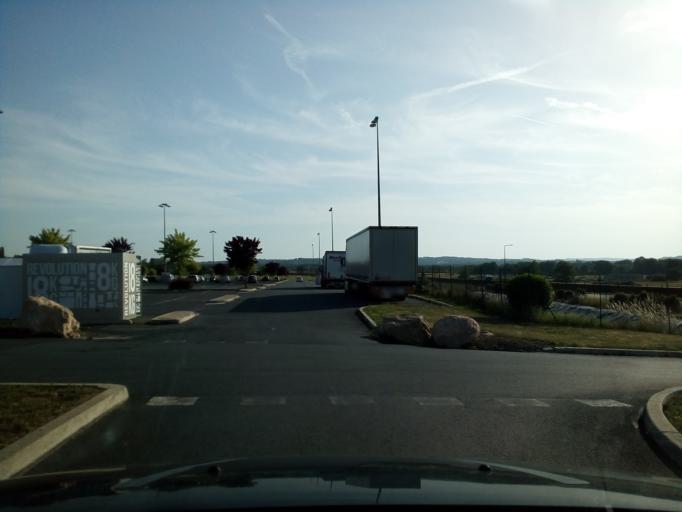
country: FR
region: Auvergne
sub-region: Departement de l'Allier
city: Domerat
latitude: 46.3665
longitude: 2.5625
